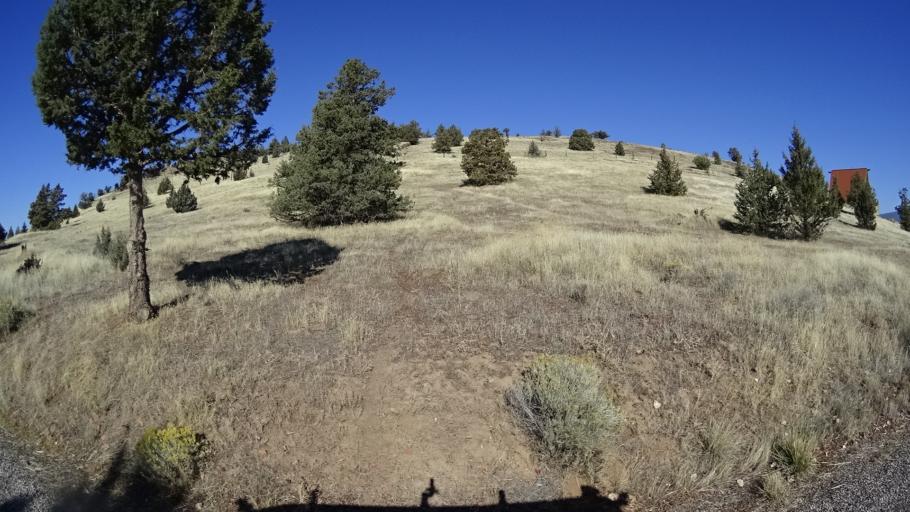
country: US
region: California
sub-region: Siskiyou County
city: Montague
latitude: 41.6591
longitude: -122.3718
